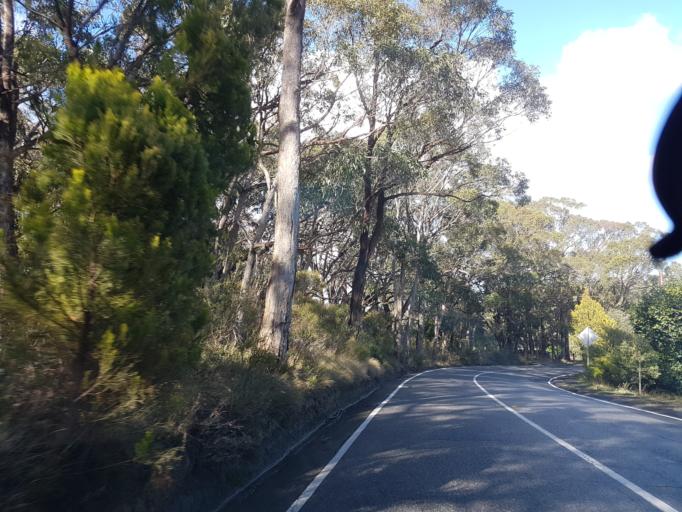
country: AU
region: South Australia
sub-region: Adelaide Hills
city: Heathfield
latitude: -35.0246
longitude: 138.7157
